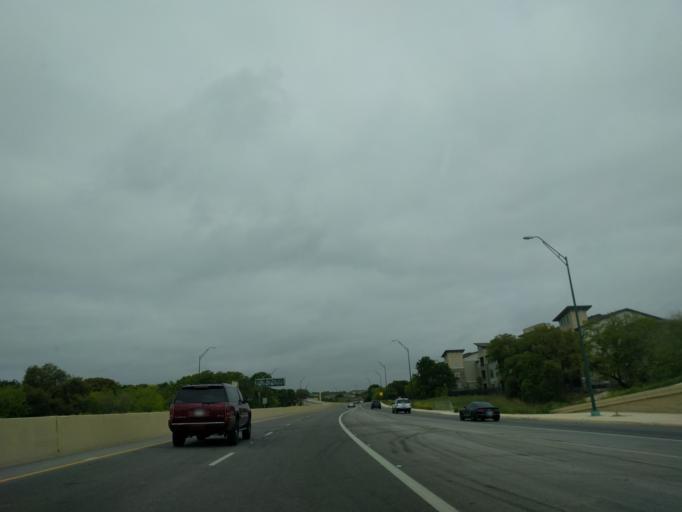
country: US
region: Texas
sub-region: Bexar County
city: Castle Hills
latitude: 29.5588
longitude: -98.5007
